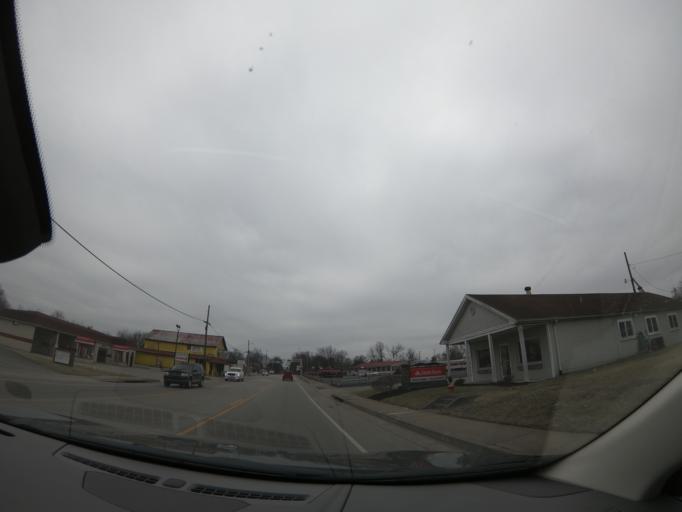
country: US
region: Kentucky
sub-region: Nelson County
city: Bardstown
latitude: 37.8183
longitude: -85.4639
